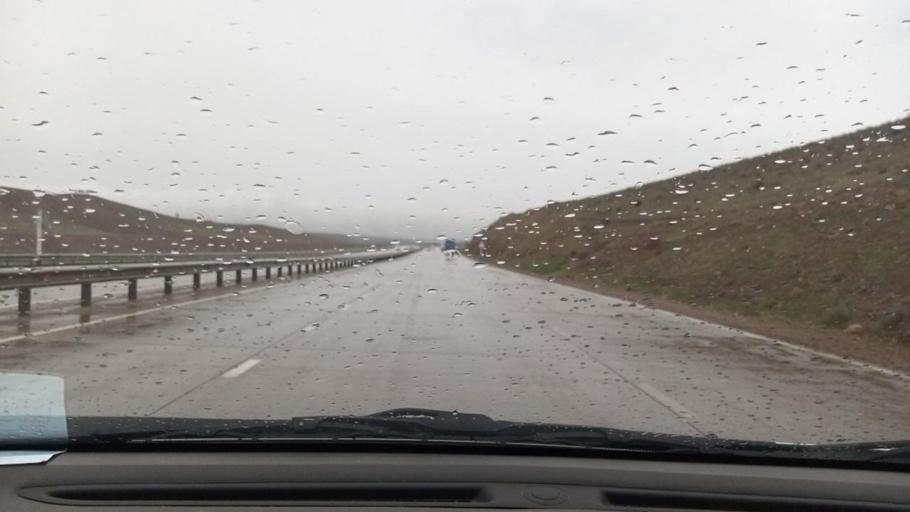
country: UZ
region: Namangan
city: Pop Shahri
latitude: 40.9293
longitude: 70.7098
